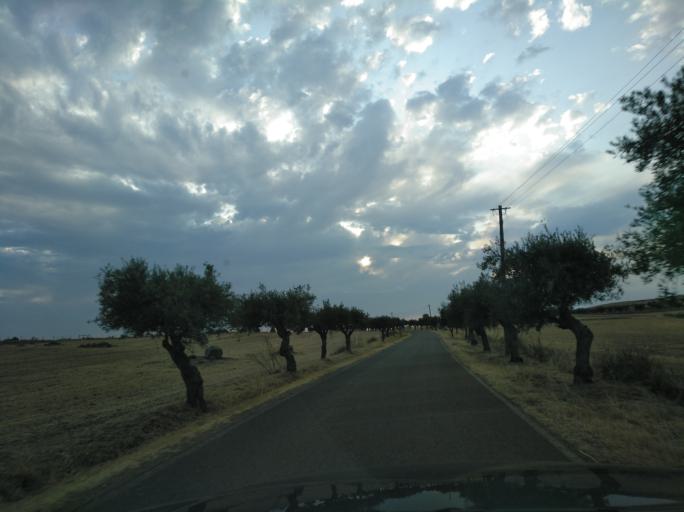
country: PT
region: Portalegre
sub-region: Campo Maior
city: Campo Maior
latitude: 39.0164
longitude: -7.0376
